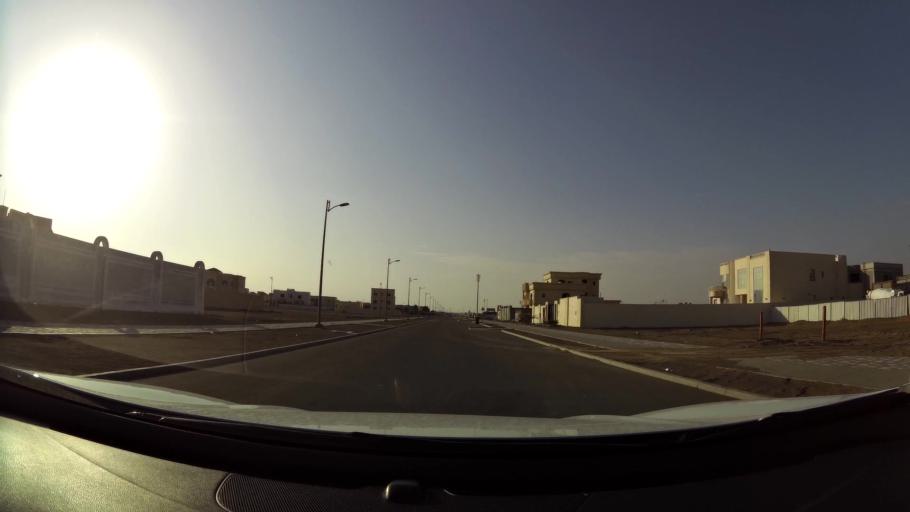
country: AE
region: Abu Dhabi
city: Al Ain
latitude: 24.0963
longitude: 55.8516
